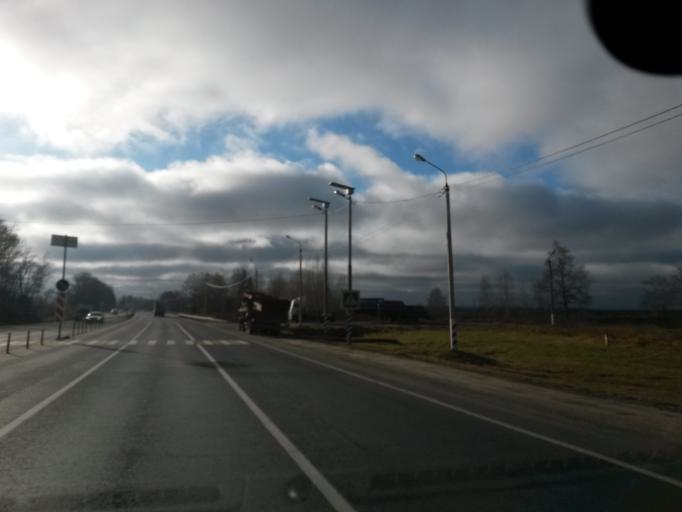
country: RU
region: Jaroslavl
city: Semibratovo
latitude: 57.3451
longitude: 39.5826
